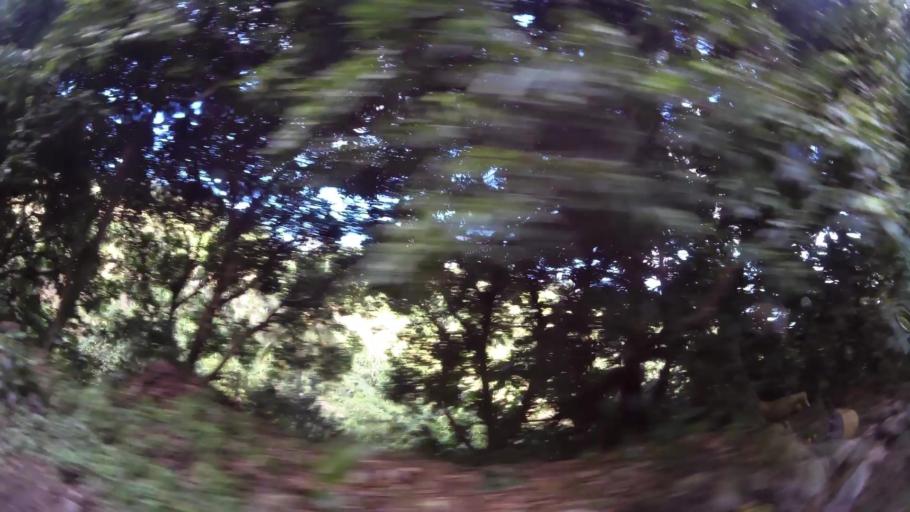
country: DM
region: Saint John
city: Portsmouth
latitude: 15.6219
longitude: -61.4164
